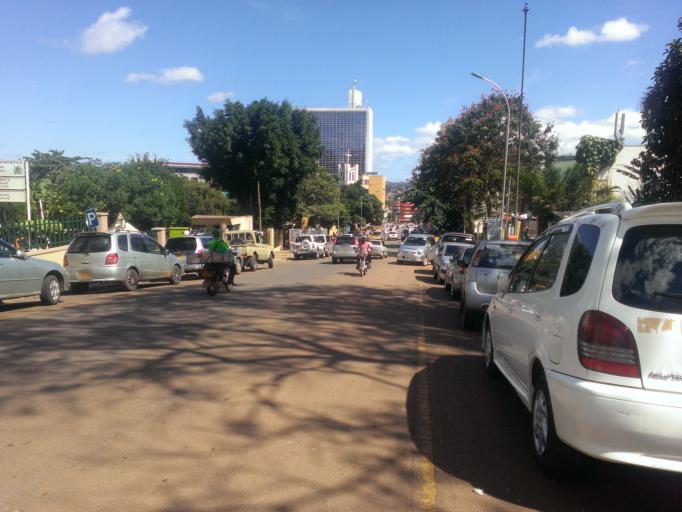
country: UG
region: Central Region
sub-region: Kampala District
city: Kampala
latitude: 0.3158
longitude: 32.5845
